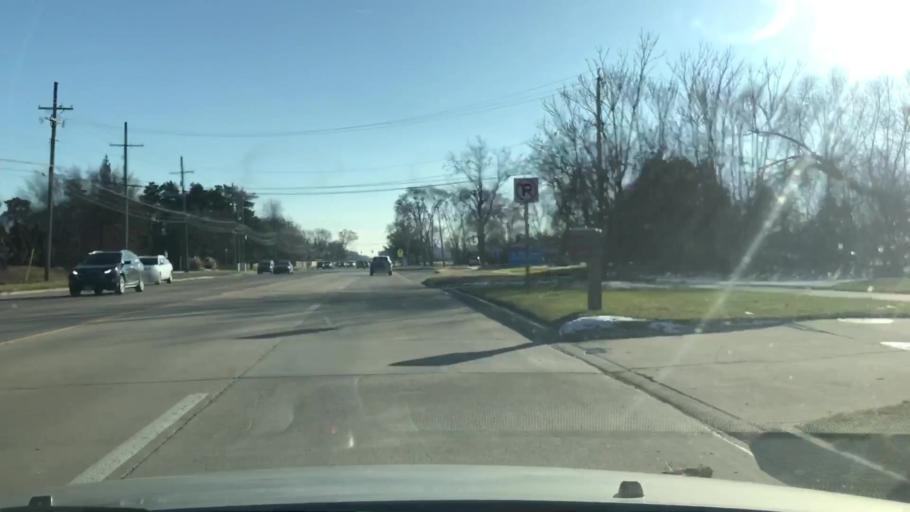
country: US
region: Michigan
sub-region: Oakland County
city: Troy
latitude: 42.5869
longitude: -83.1094
